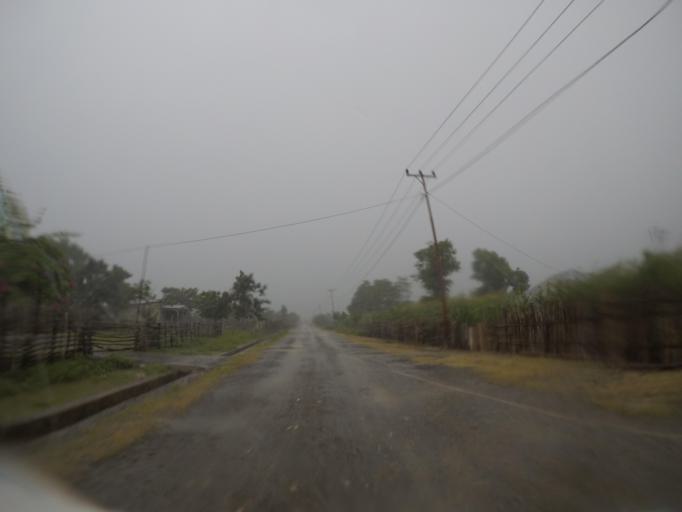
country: TL
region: Bobonaro
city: Maliana
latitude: -8.8651
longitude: 125.1036
